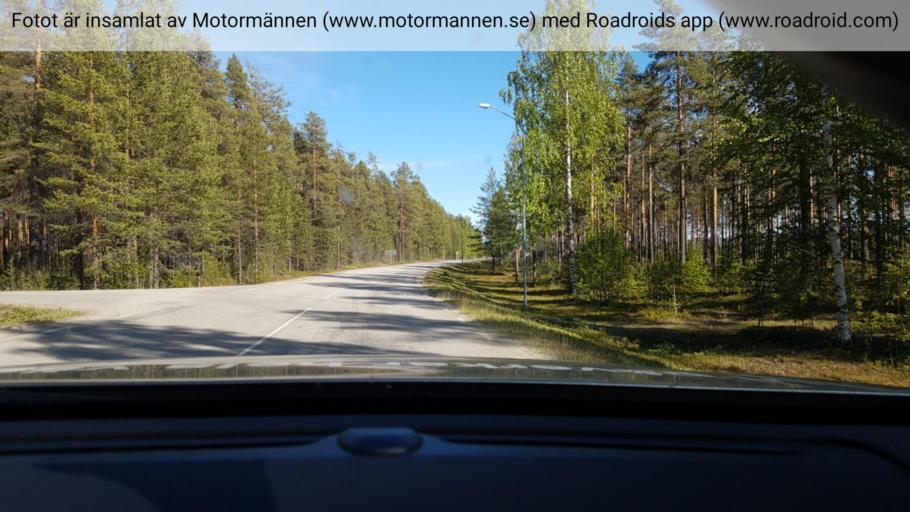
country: SE
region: Vaesterbotten
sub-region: Lycksele Kommun
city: Lycksele
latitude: 64.8124
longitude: 18.9150
